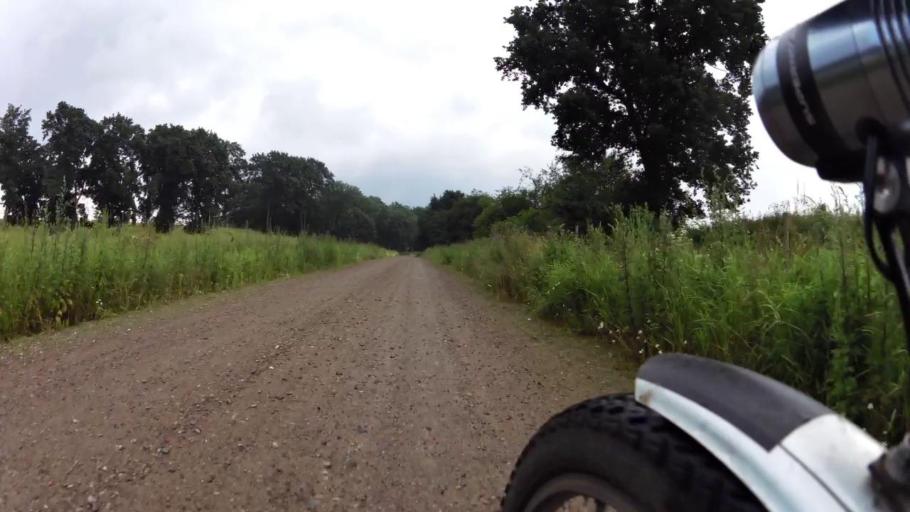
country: PL
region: West Pomeranian Voivodeship
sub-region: Powiat lobeski
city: Lobez
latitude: 53.7258
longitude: 15.6344
